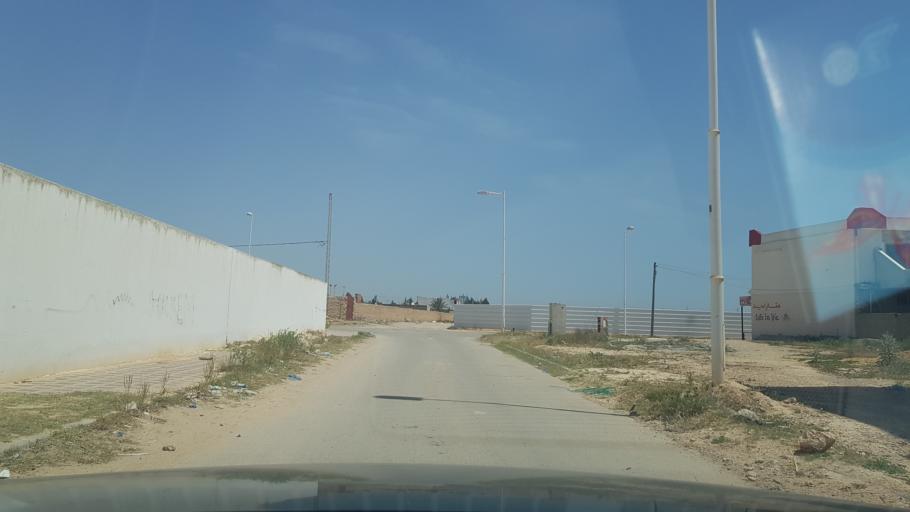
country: TN
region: Safaqis
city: Al Qarmadah
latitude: 34.8406
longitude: 10.7575
